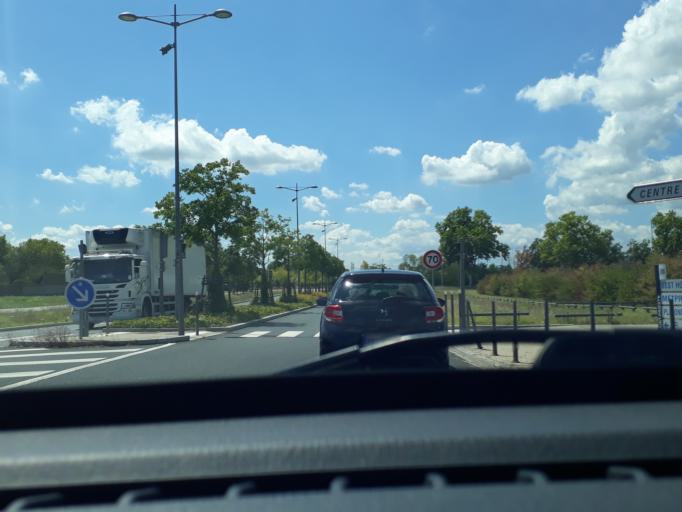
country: FR
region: Rhone-Alpes
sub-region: Departement du Rhone
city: Saint-Priest
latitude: 45.7048
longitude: 4.9155
